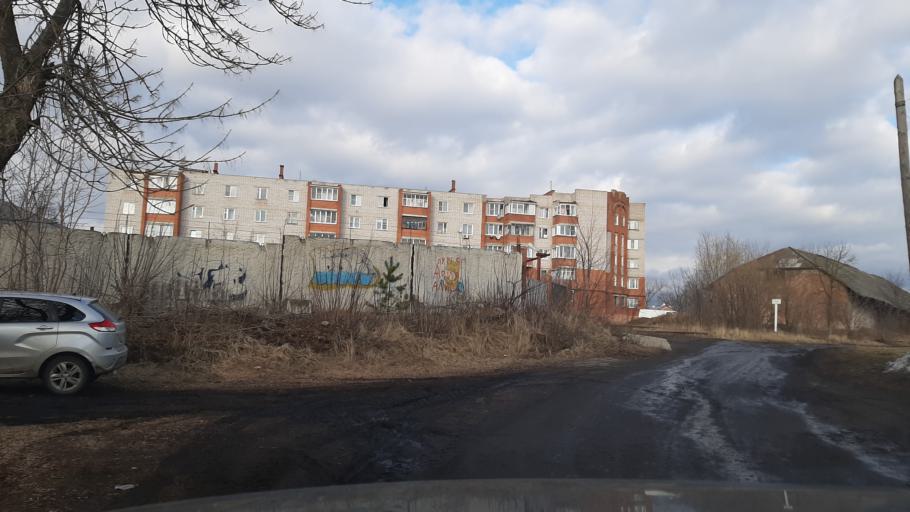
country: RU
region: Ivanovo
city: Teykovo
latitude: 56.8540
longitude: 40.5583
